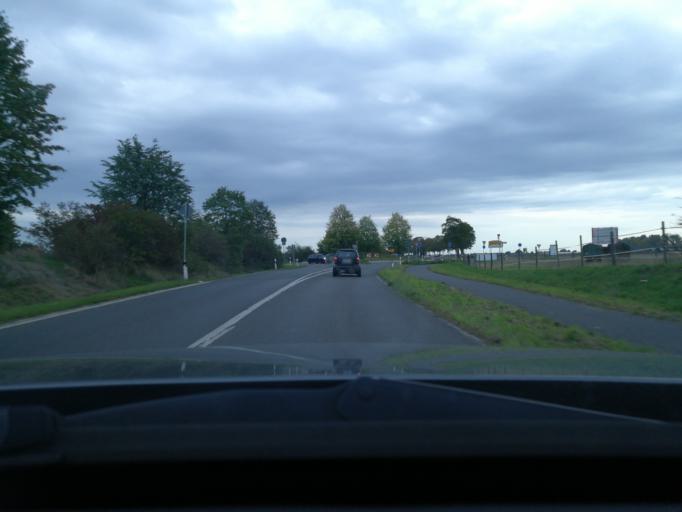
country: DE
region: North Rhine-Westphalia
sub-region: Regierungsbezirk Dusseldorf
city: Dormagen
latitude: 51.1344
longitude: 6.7517
